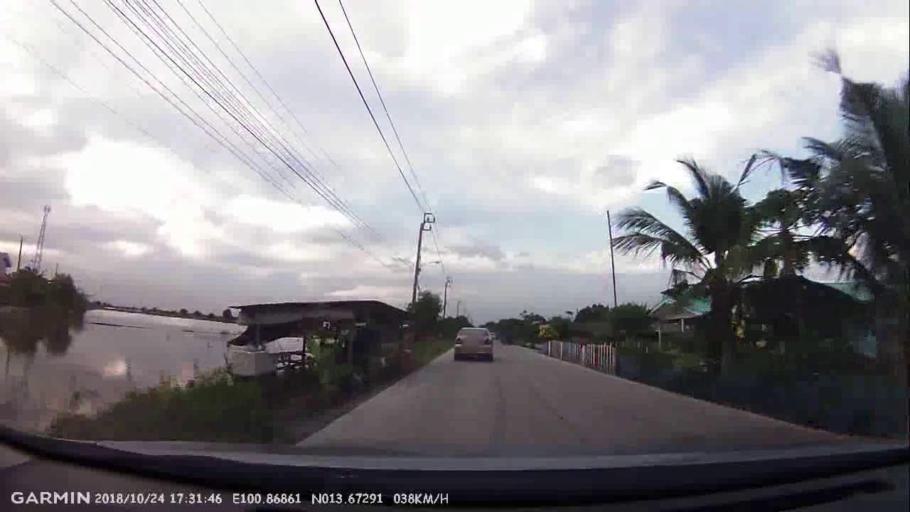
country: TH
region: Samut Prakan
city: Ban Khlong Bang Sao Thong
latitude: 13.6730
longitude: 100.8686
